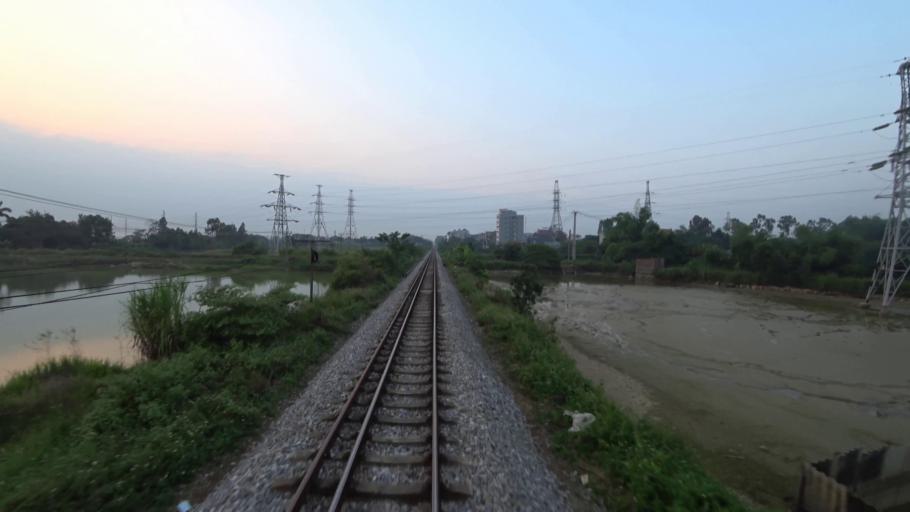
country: VN
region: Ha Noi
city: Dong Anh
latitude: 21.1471
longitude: 105.8592
